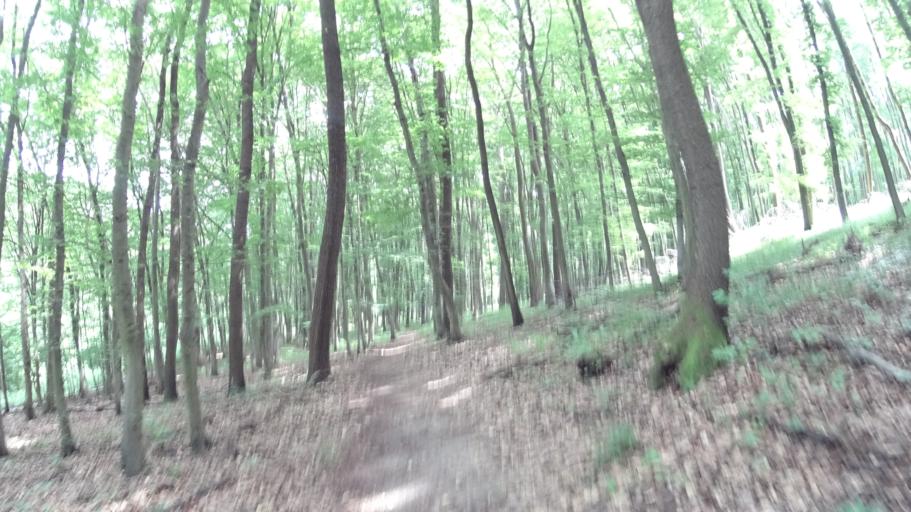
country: HU
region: Pest
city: Nagymaros
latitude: 47.8010
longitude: 18.9309
